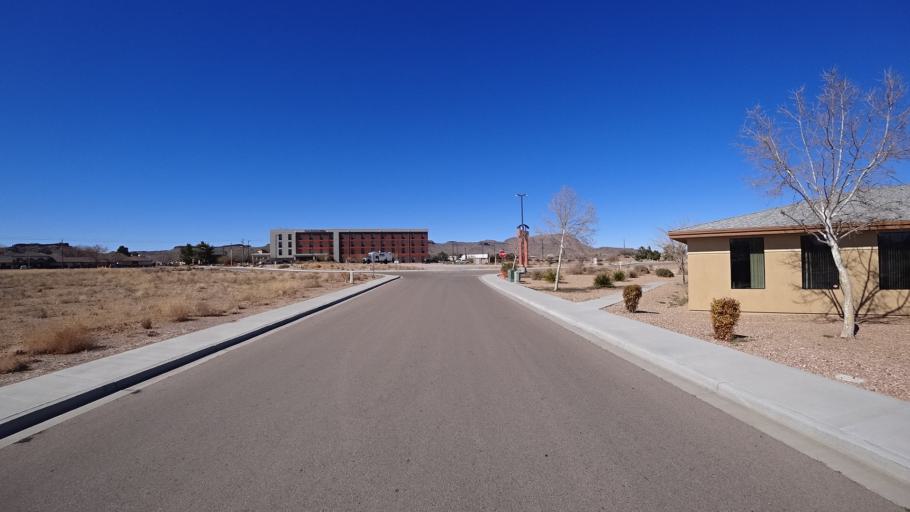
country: US
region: Arizona
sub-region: Mohave County
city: Kingman
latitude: 35.2147
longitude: -114.0384
